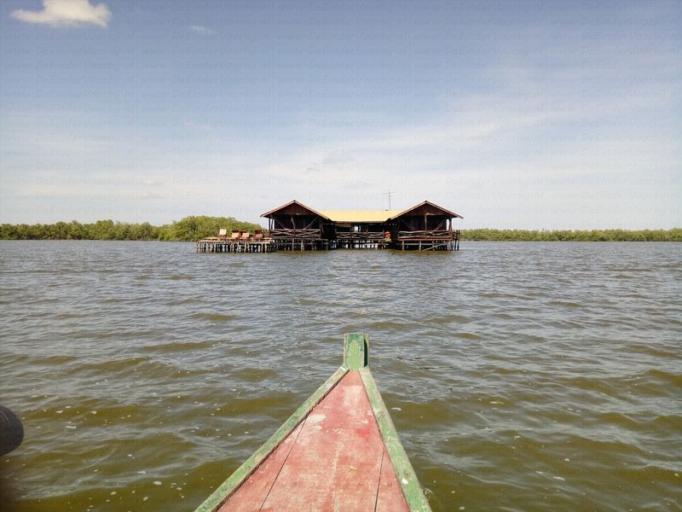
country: SR
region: Nickerie
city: Nieuw Nickerie
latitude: 5.9589
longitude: -56.8622
